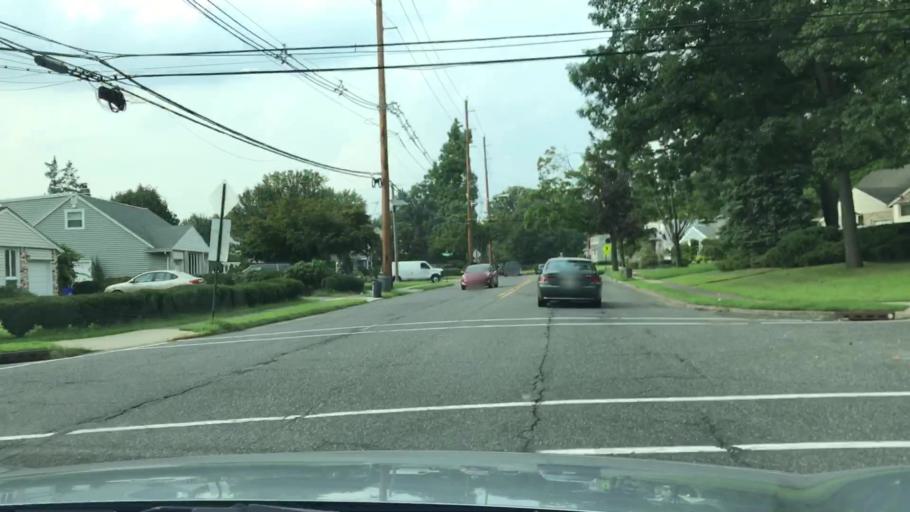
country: US
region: New Jersey
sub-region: Bergen County
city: New Milford
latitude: 40.9211
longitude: -74.0174
